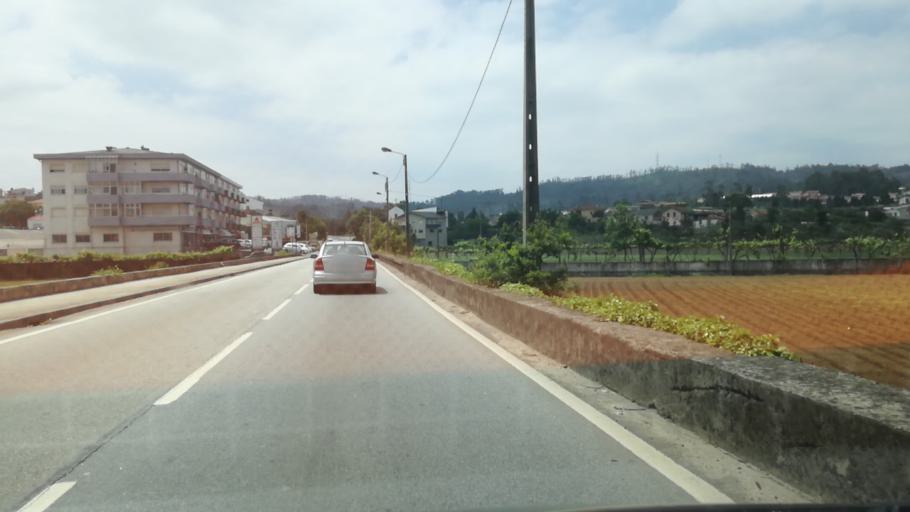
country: PT
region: Porto
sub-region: Trofa
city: Bougado
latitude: 41.3217
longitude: -8.5730
